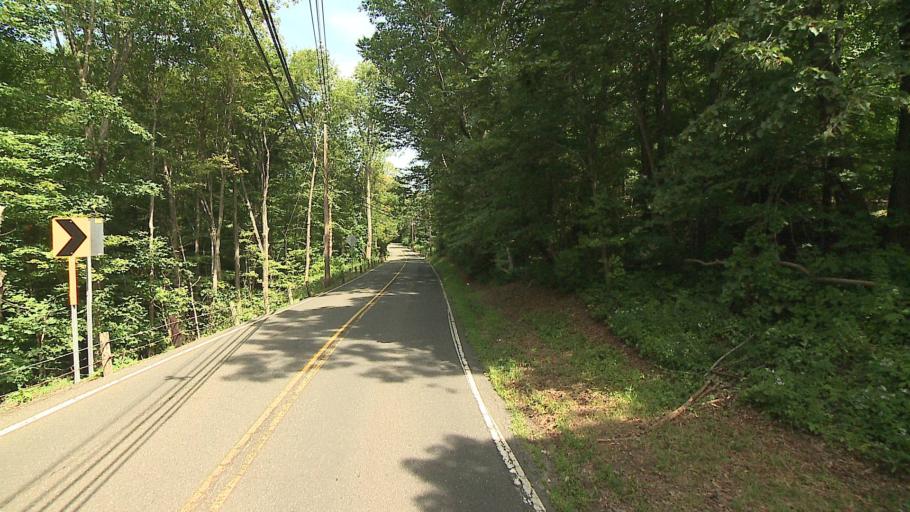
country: US
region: Connecticut
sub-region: Litchfield County
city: Bethlehem Village
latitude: 41.6368
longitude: -73.2200
